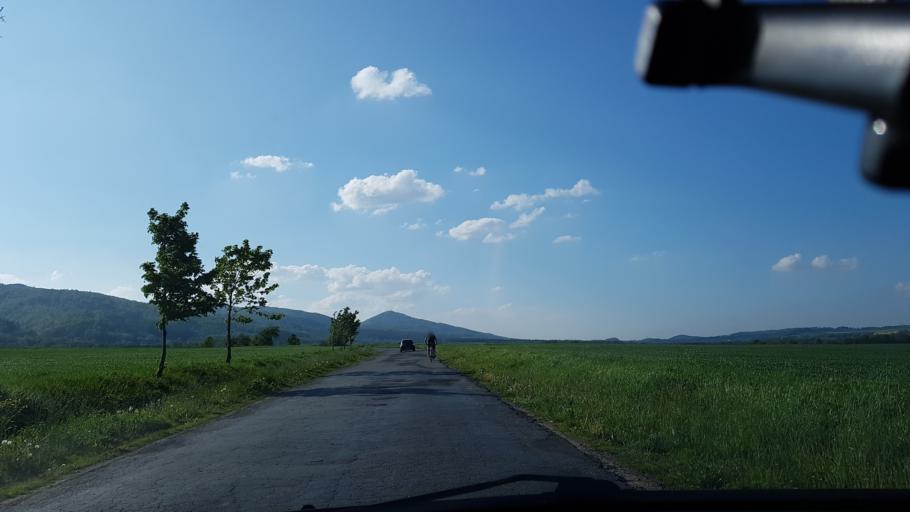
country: PL
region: Lower Silesian Voivodeship
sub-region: Powiat zabkowicki
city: Budzow
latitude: 50.5844
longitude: 16.6692
